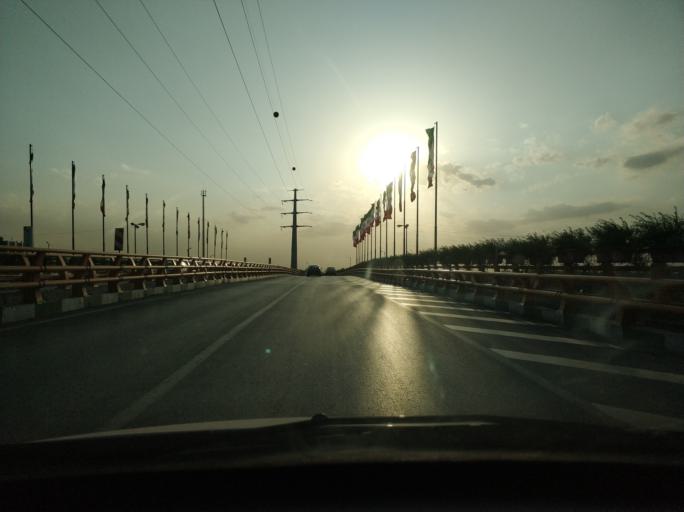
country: IR
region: Razavi Khorasan
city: Mashhad
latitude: 36.3400
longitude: 59.5480
